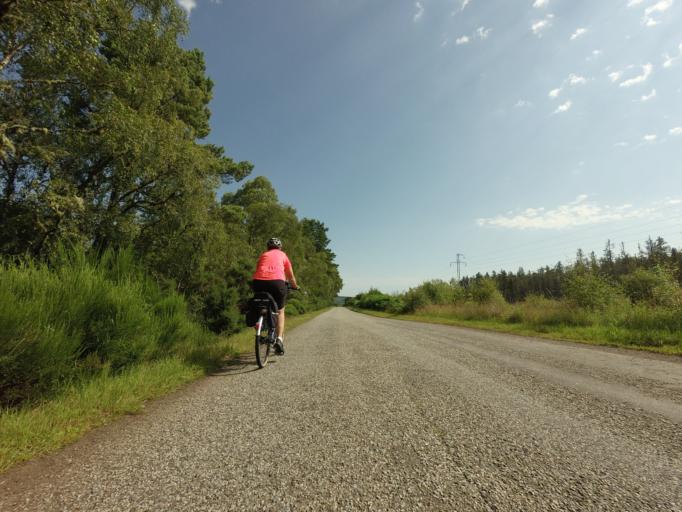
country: GB
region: Scotland
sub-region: Highland
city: Invergordon
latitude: 57.7404
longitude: -4.1819
